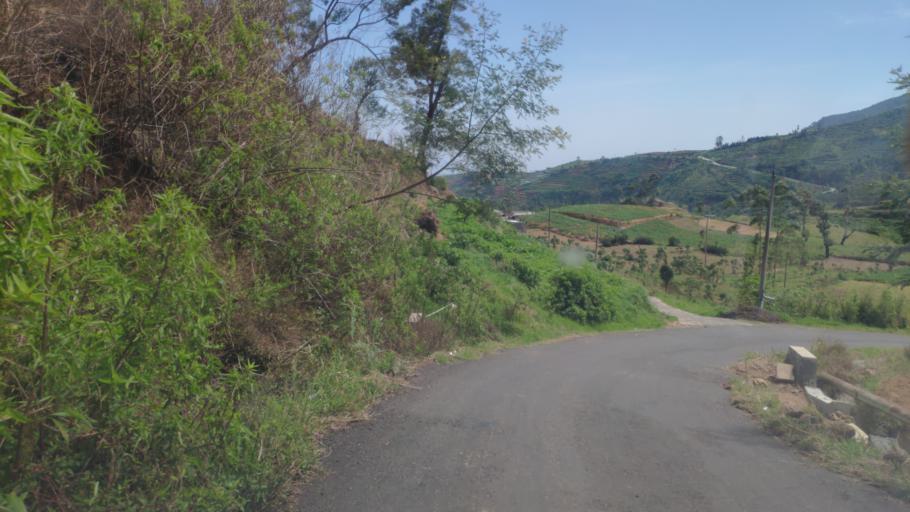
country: ID
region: Central Java
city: Wonosobo
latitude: -7.1859
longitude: 109.8846
